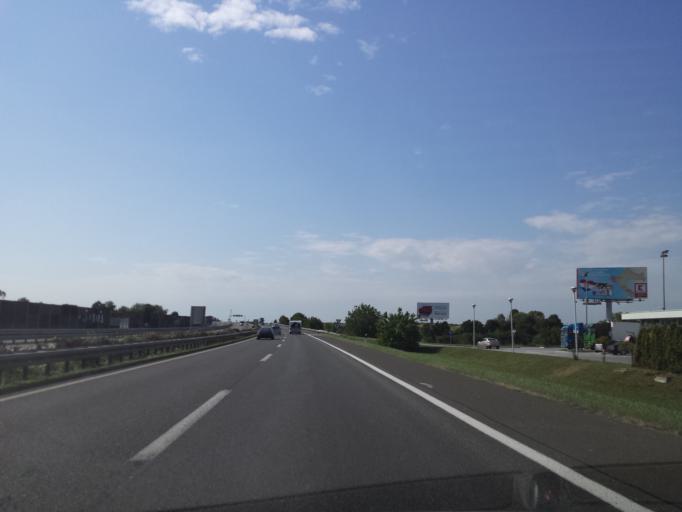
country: HR
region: Grad Zagreb
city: Brezovica
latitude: 45.7453
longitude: 15.8814
